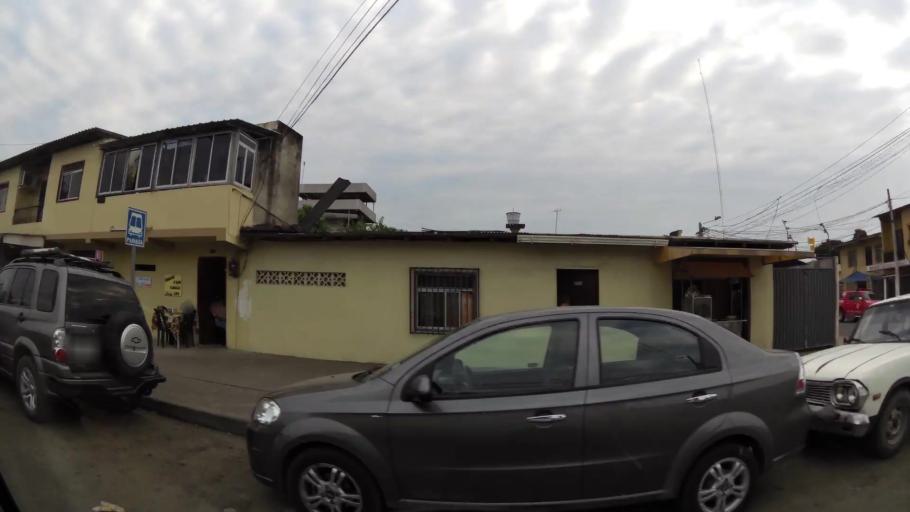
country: EC
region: El Oro
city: Machala
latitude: -3.2504
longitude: -79.9589
